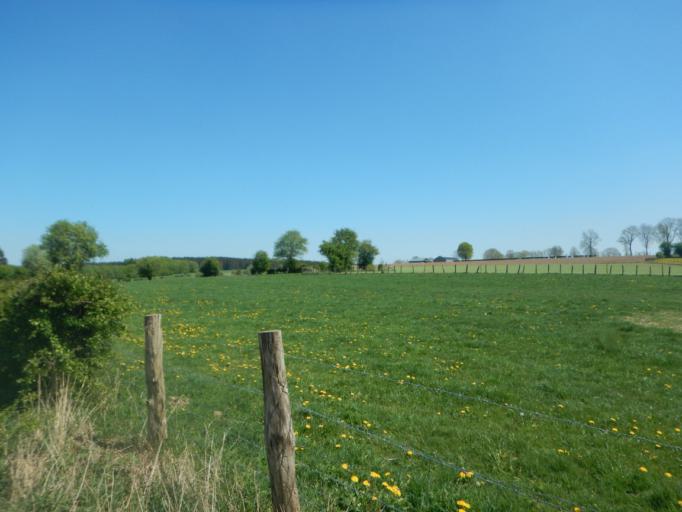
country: LU
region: Diekirch
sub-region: Canton de Clervaux
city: Troisvierges
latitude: 50.1480
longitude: 6.0257
